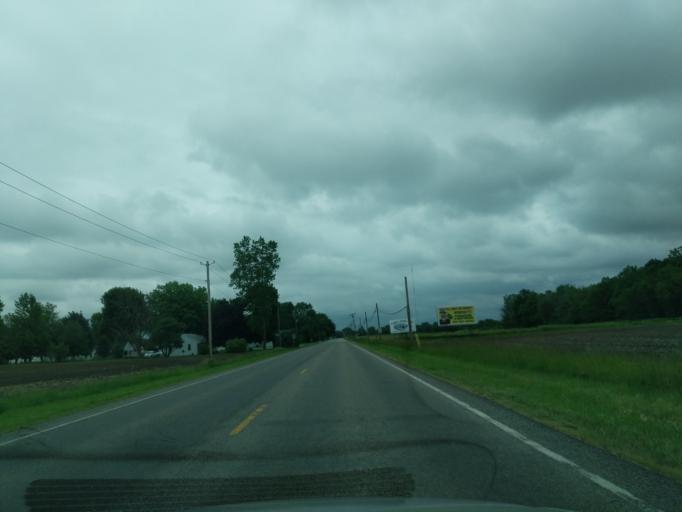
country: US
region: Indiana
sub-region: Madison County
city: Elwood
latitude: 40.2768
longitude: -85.8716
